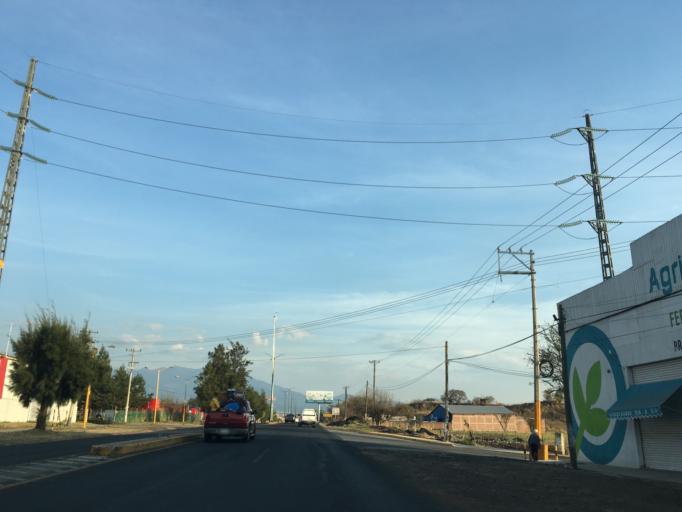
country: MX
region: Michoacan
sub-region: Los Reyes
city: La Higuerita (Colonia San Rafael)
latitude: 19.6033
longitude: -102.4773
